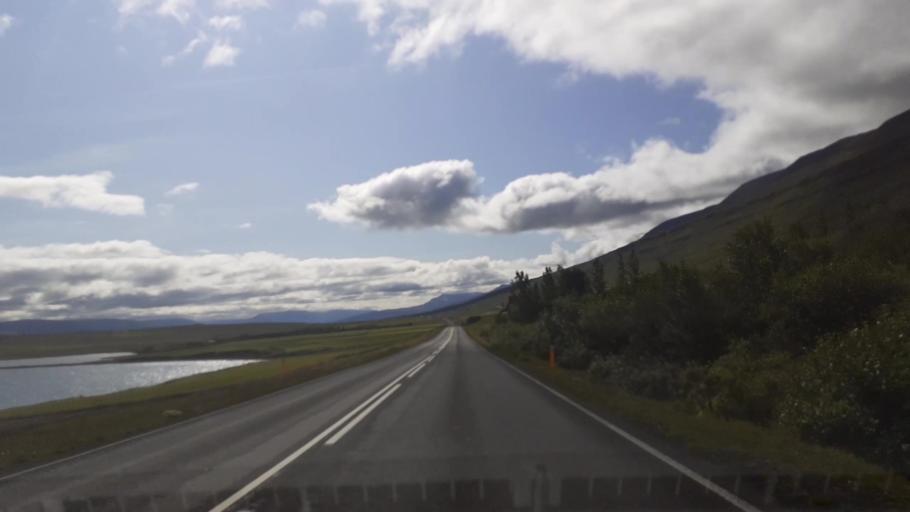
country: IS
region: Northeast
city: Akureyri
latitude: 65.8732
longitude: -18.2639
